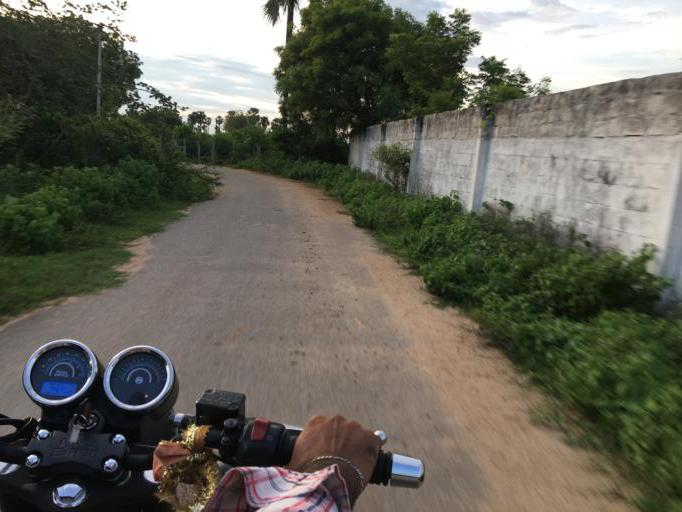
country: IN
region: Telangana
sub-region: Nalgonda
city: Nalgonda
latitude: 17.1754
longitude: 79.4163
